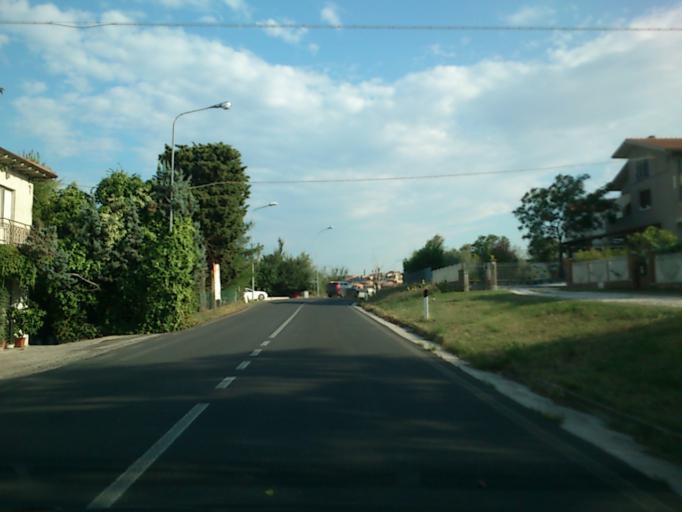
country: IT
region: The Marches
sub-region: Provincia di Pesaro e Urbino
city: San Costanzo
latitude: 43.7792
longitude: 13.0753
